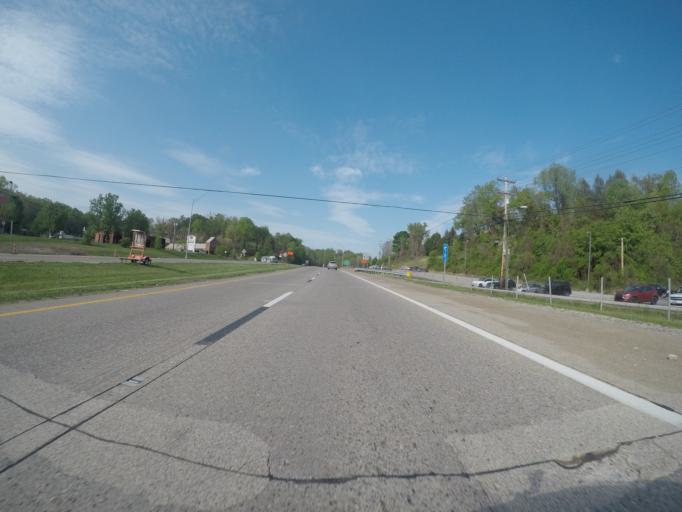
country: US
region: West Virginia
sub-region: Kanawha County
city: South Charleston
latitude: 38.3425
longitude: -81.6772
